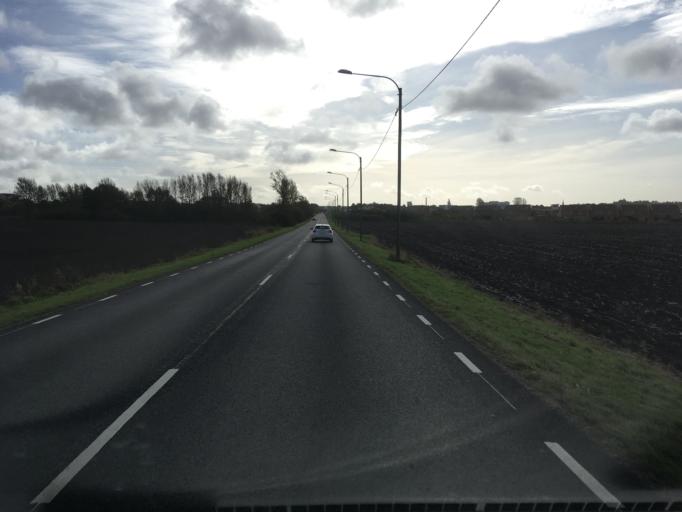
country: SE
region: Skane
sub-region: Lunds Kommun
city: Lund
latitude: 55.7345
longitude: 13.1994
